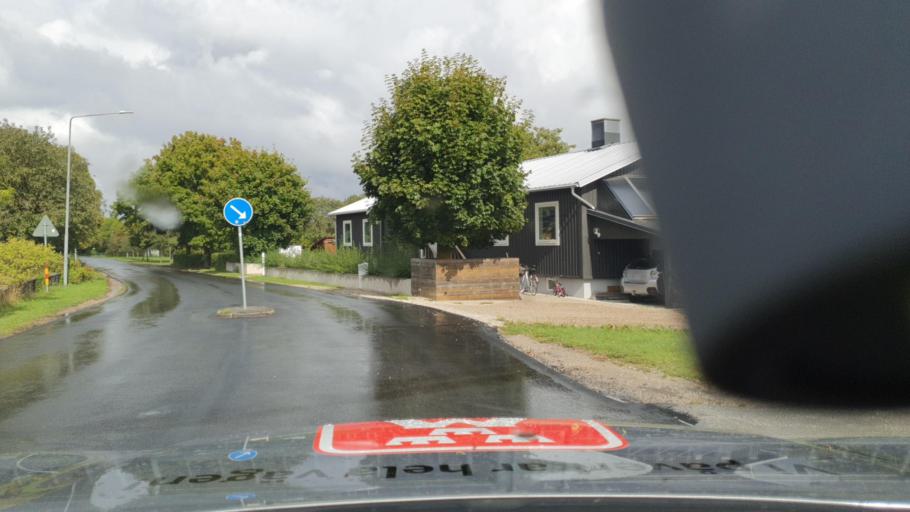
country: SE
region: Gotland
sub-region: Gotland
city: Slite
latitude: 57.8581
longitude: 19.0575
